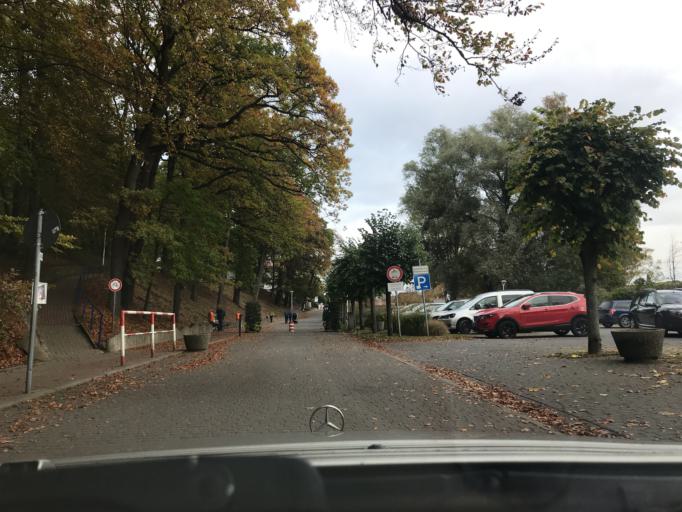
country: DE
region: Mecklenburg-Vorpommern
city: Loddin
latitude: 54.0402
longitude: 14.0273
